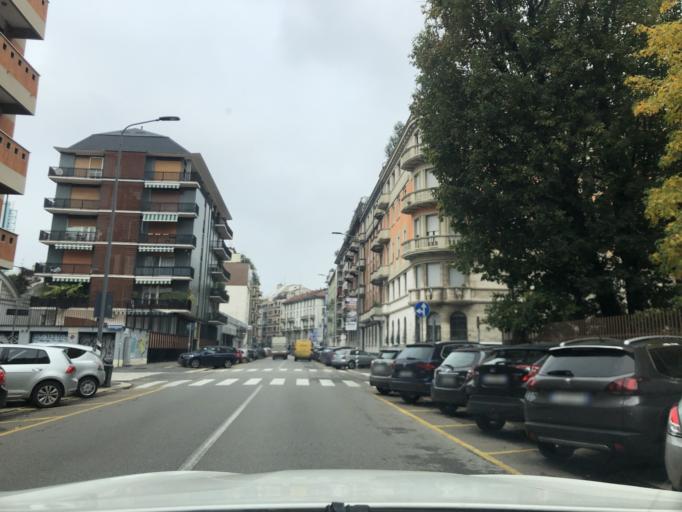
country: IT
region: Lombardy
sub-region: Citta metropolitana di Milano
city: Milano
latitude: 45.4569
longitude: 9.2096
